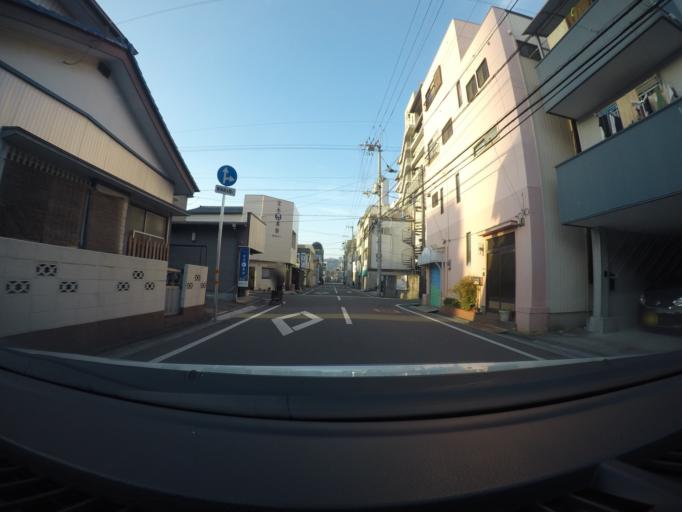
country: JP
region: Kochi
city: Kochi-shi
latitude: 33.5575
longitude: 133.5536
